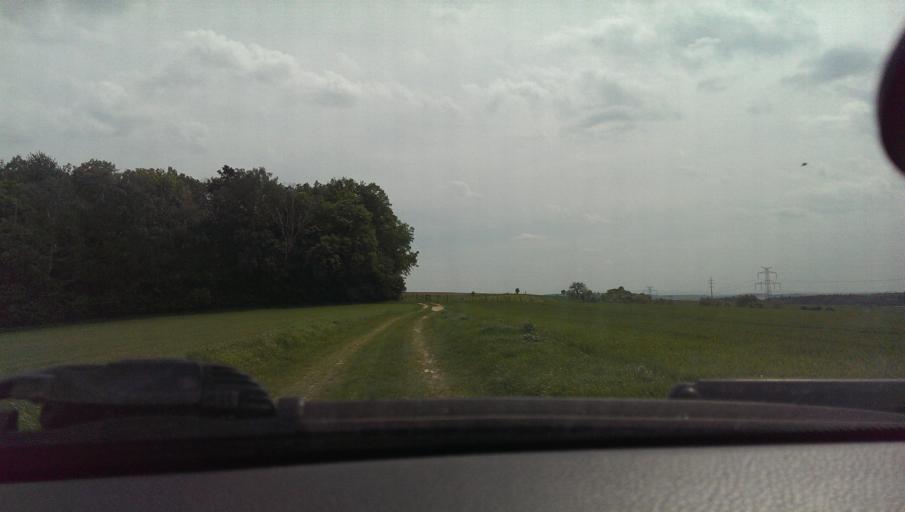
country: CZ
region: Zlin
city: Tlumacov
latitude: 49.2605
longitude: 17.5330
